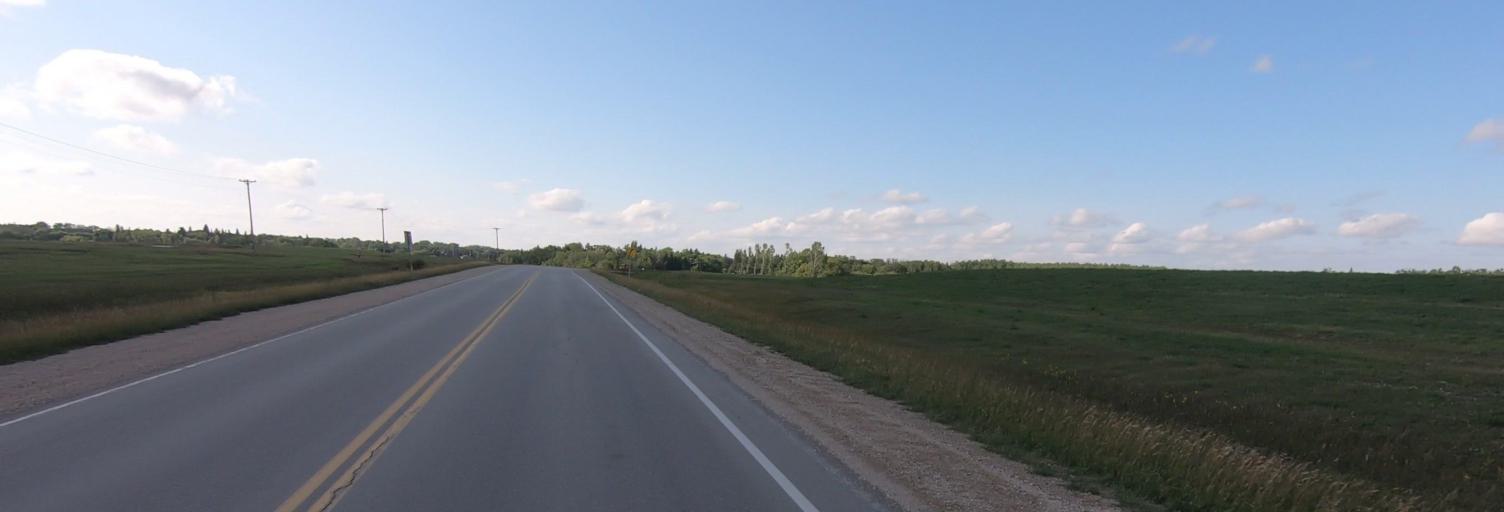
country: CA
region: Manitoba
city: Selkirk
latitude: 50.0908
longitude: -96.9292
